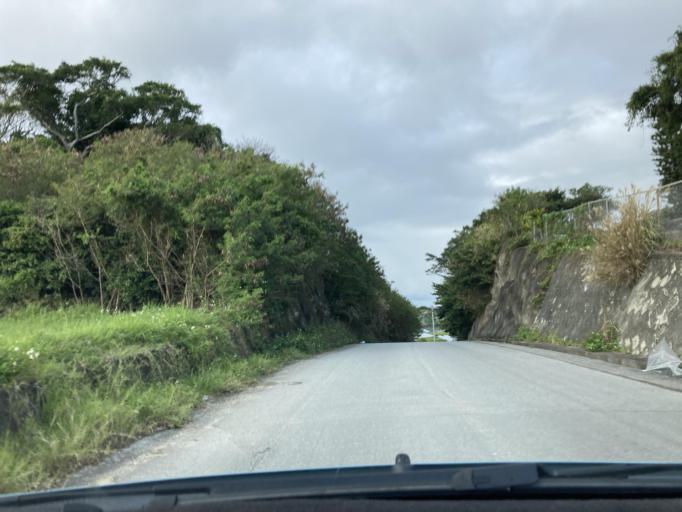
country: JP
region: Okinawa
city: Itoman
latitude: 26.1218
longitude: 127.6865
